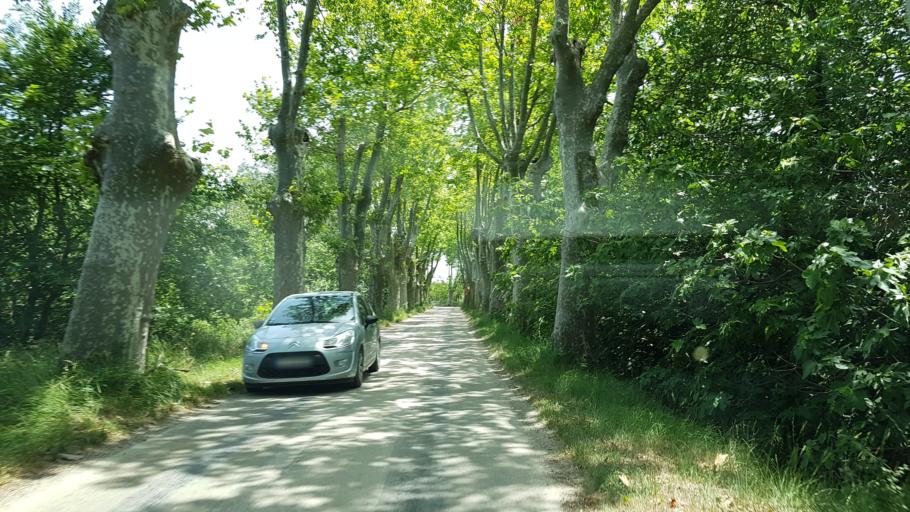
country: FR
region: Provence-Alpes-Cote d'Azur
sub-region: Departement des Bouches-du-Rhone
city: Port-Saint-Louis-du-Rhone
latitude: 43.4487
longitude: 4.6610
